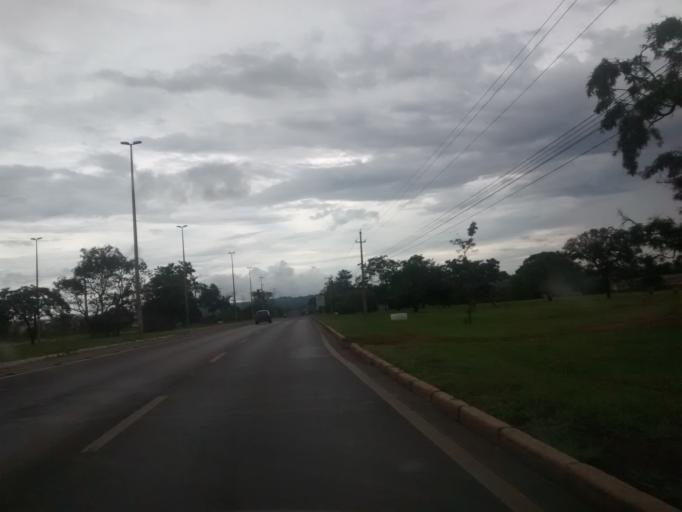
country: BR
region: Federal District
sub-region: Brasilia
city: Brasilia
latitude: -15.7729
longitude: -47.8637
